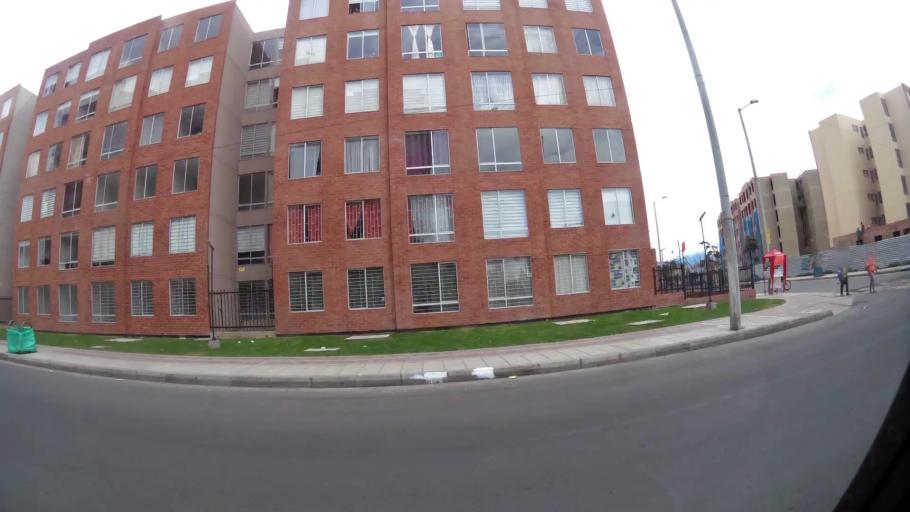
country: CO
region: Cundinamarca
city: Funza
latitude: 4.7188
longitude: -74.1288
